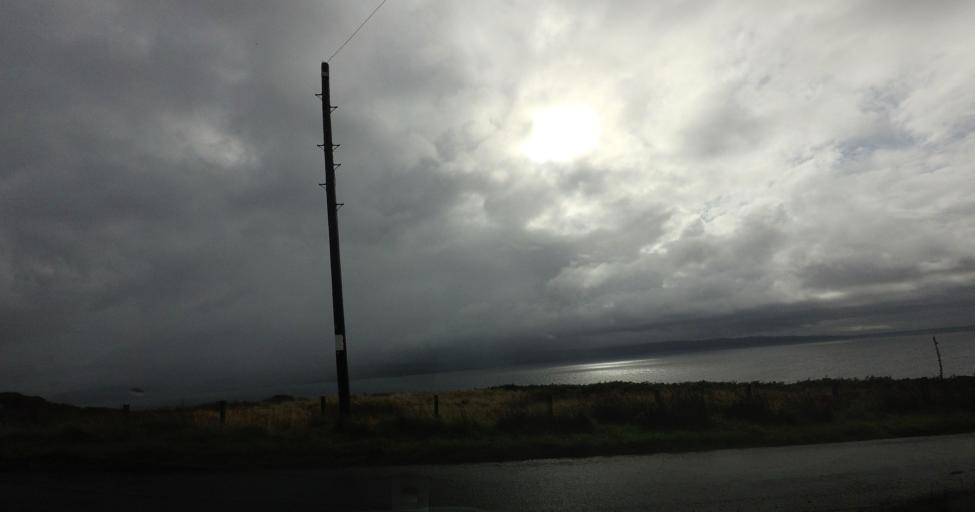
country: GB
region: Scotland
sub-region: Highland
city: Isle of Skye
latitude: 57.1401
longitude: -6.0742
